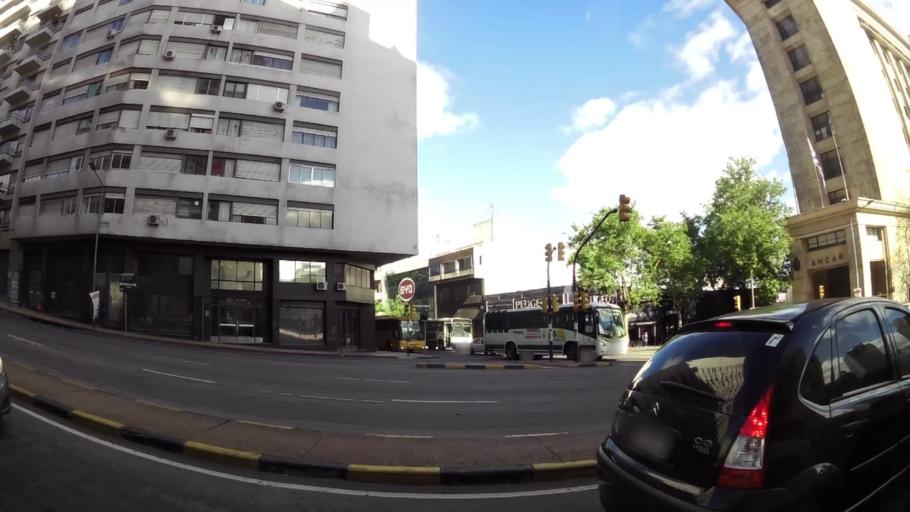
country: UY
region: Montevideo
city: Montevideo
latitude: -34.9024
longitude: -56.1926
